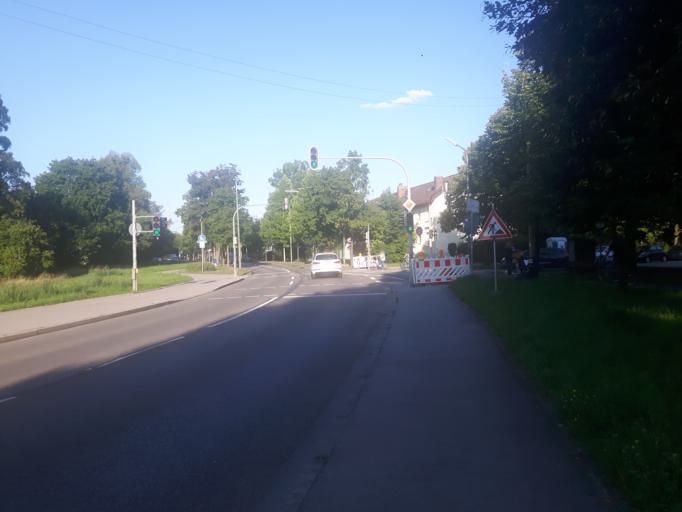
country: DE
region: Bavaria
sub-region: Upper Bavaria
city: Pasing
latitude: 48.1677
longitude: 11.5161
